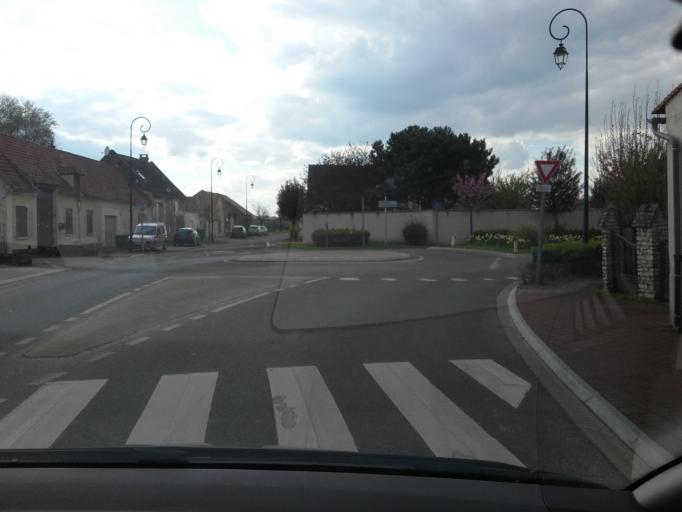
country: FR
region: Picardie
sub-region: Departement de l'Oise
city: Grandfresnoy
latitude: 49.3786
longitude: 2.6516
